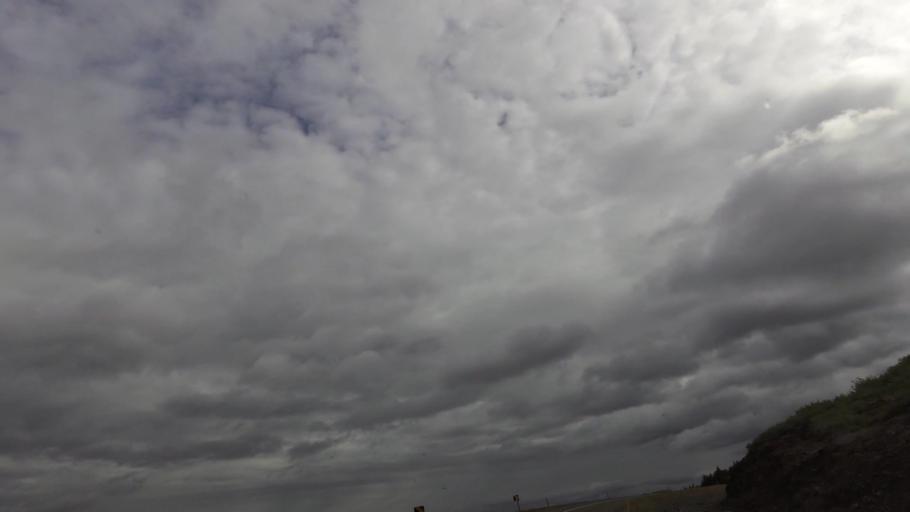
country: IS
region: West
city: Stykkisholmur
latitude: 65.5209
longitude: -22.1166
